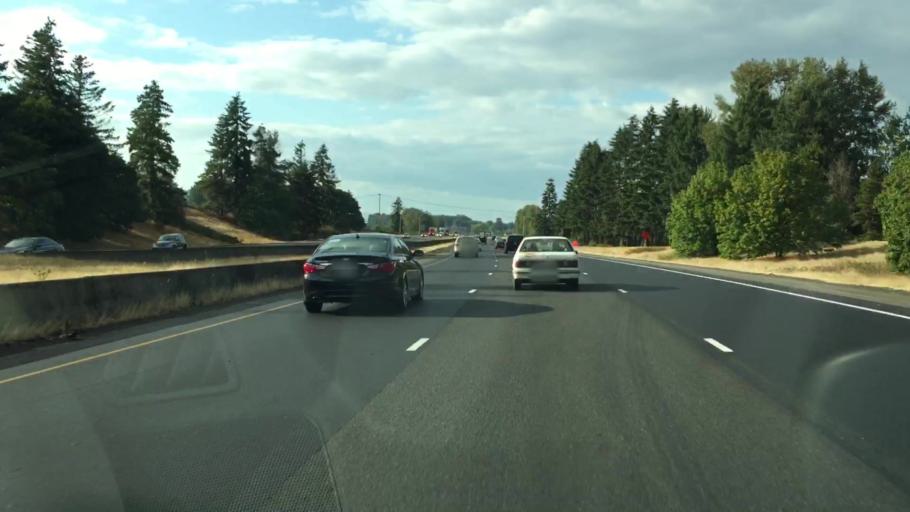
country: US
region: Washington
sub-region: Cowlitz County
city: Kalama
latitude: 46.0188
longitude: -122.8496
